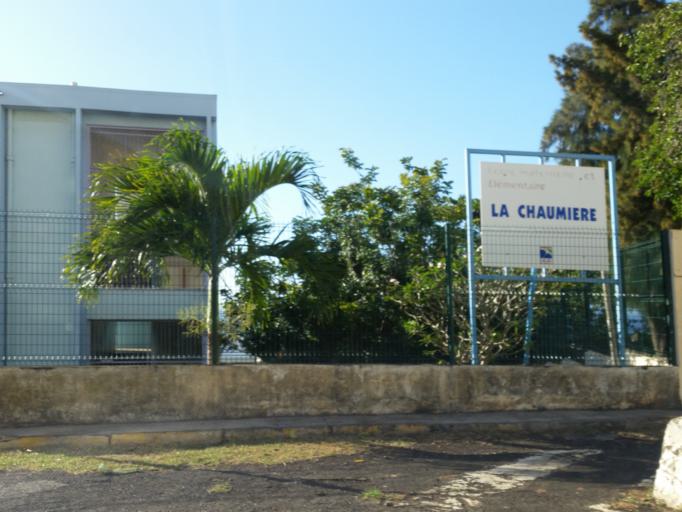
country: RE
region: Reunion
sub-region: Reunion
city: Saint-Denis
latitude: -20.8989
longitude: 55.4625
